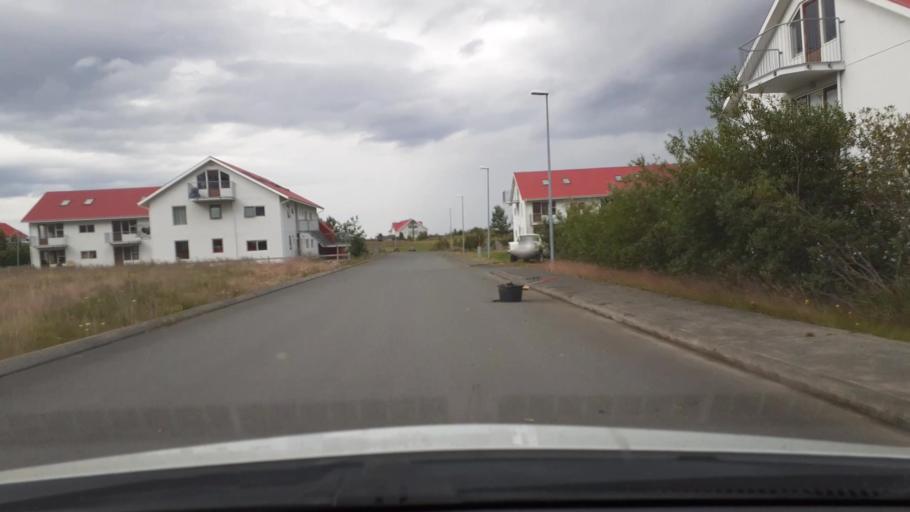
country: IS
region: West
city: Borgarnes
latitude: 64.5604
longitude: -21.7652
